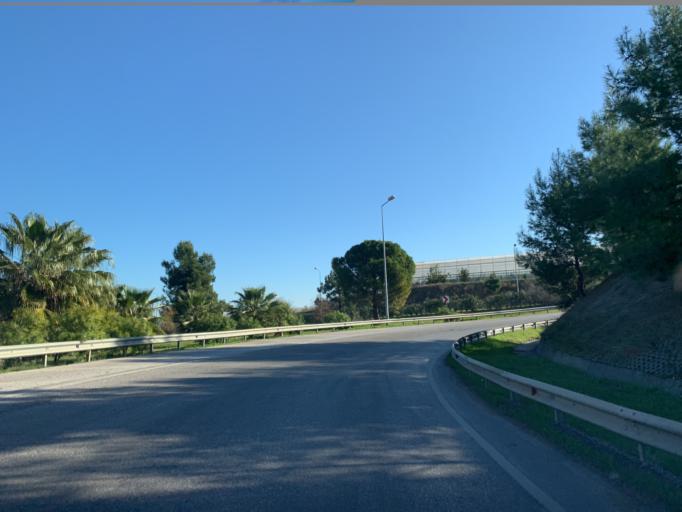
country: TR
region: Antalya
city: Aksu
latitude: 36.9454
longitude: 30.8320
